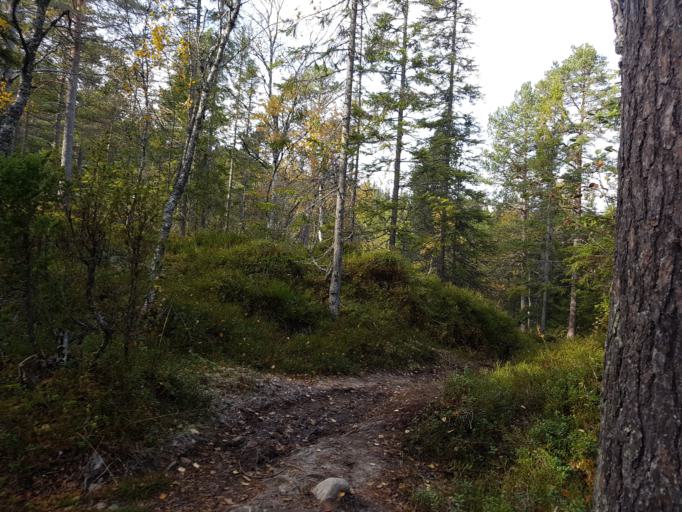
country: NO
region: Sor-Trondelag
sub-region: Trondheim
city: Trondheim
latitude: 63.4478
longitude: 10.2719
